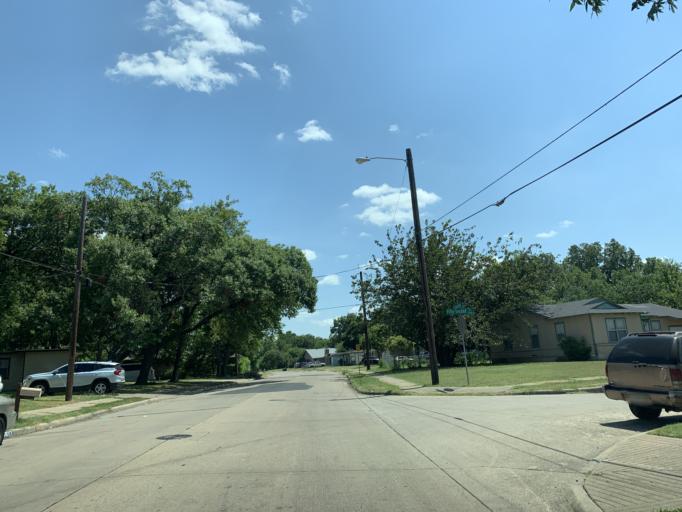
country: US
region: Texas
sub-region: Dallas County
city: Hutchins
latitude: 32.7020
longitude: -96.7643
